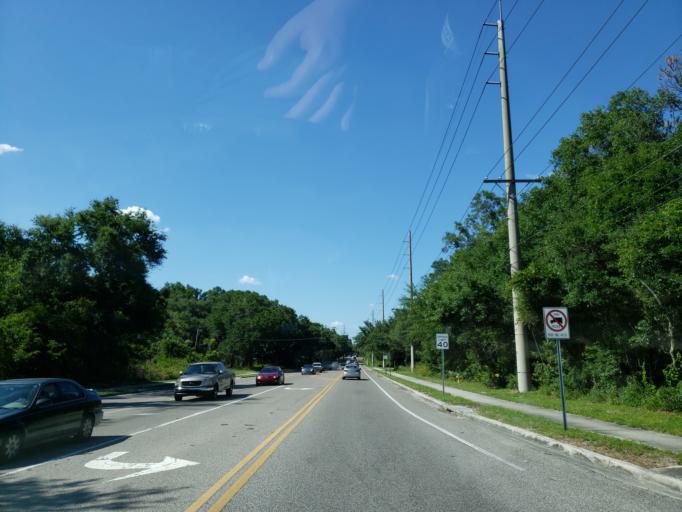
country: US
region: Florida
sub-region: Hillsborough County
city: Mango
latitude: 27.9772
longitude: -82.3105
